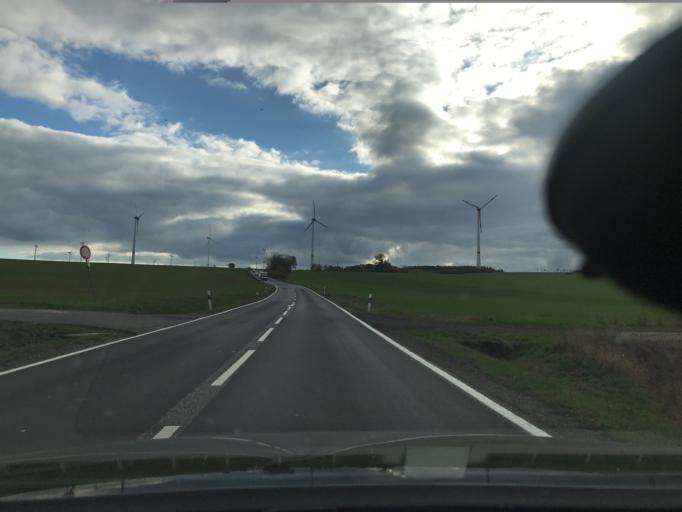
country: DE
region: Thuringia
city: Mihla
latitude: 51.0633
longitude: 10.3239
